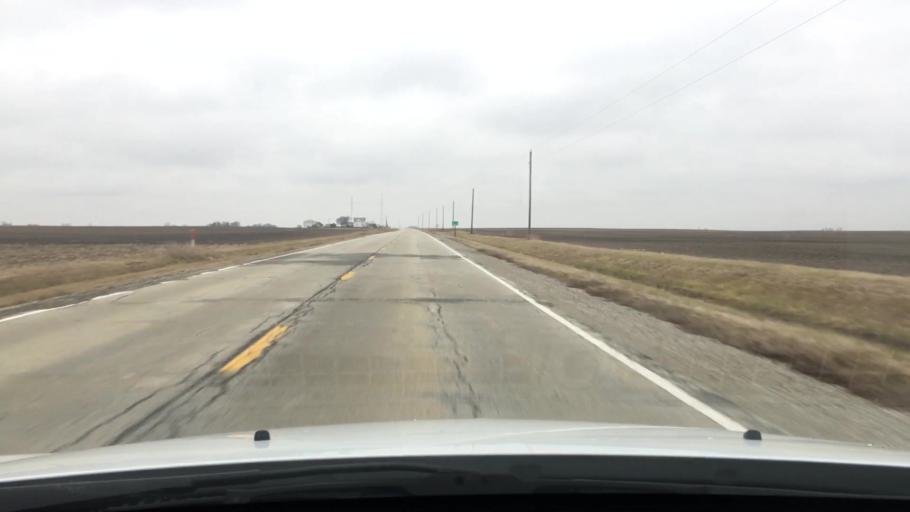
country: US
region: Illinois
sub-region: Iroquois County
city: Clifton
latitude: 40.8838
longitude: -87.9764
